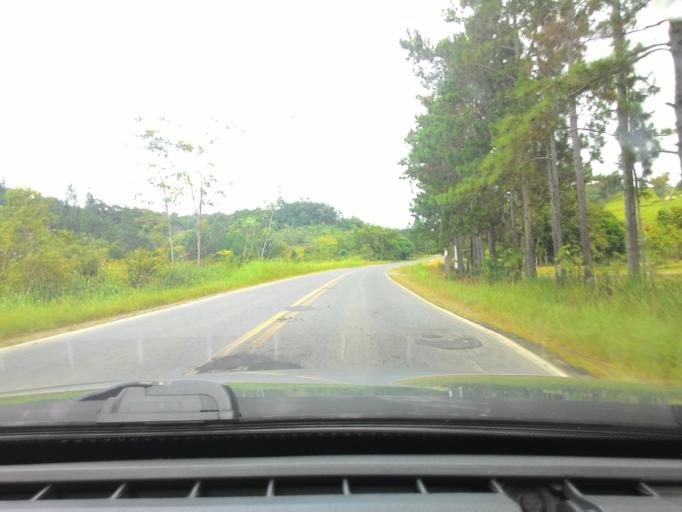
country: BR
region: Sao Paulo
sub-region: Pariquera-Acu
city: Pariquera Acu
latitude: -24.7328
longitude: -47.8372
